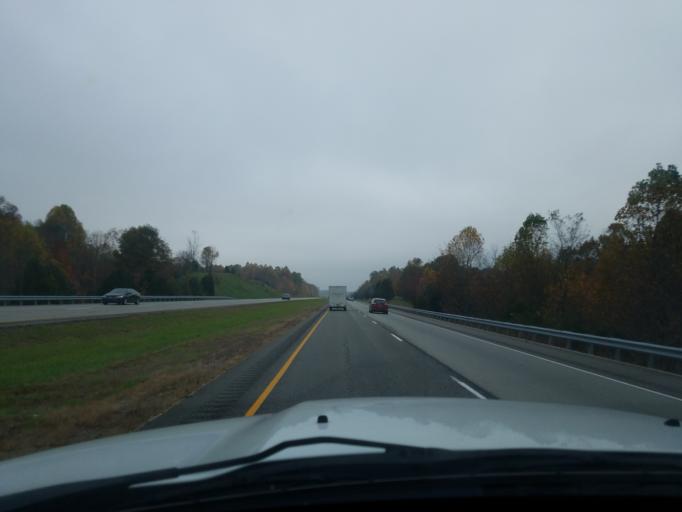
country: US
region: Kentucky
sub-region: Hardin County
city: Elizabethtown
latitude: 37.6331
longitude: -85.8265
